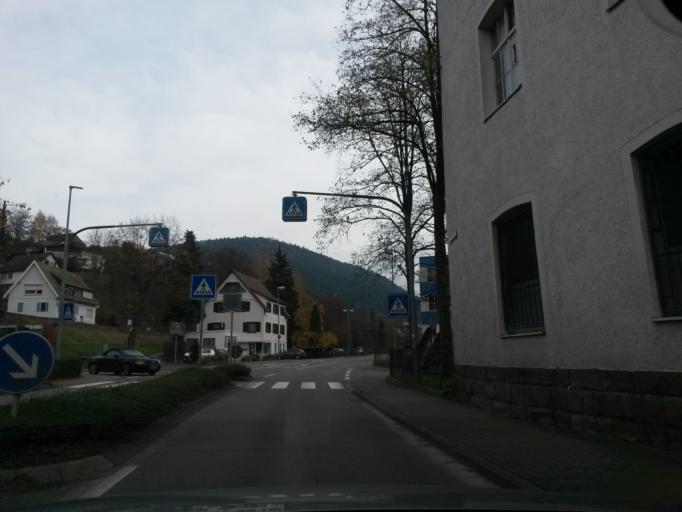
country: DE
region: Baden-Wuerttemberg
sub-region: Karlsruhe Region
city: Alpirsbach
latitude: 48.3463
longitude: 8.4061
